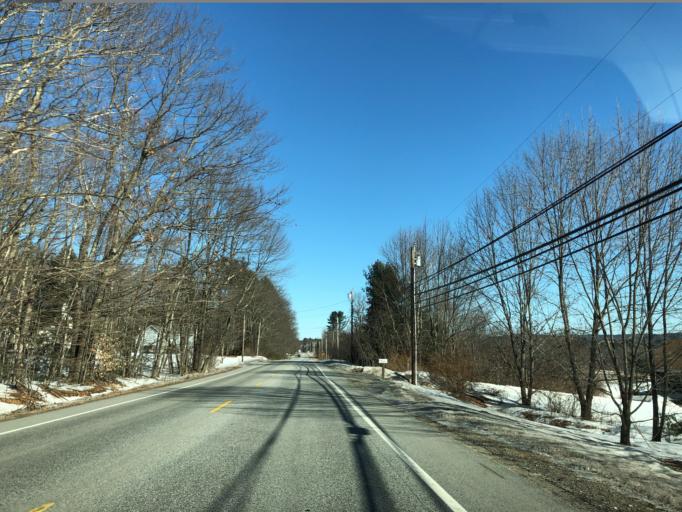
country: US
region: Maine
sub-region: Cumberland County
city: South Windham
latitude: 43.7727
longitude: -70.4193
